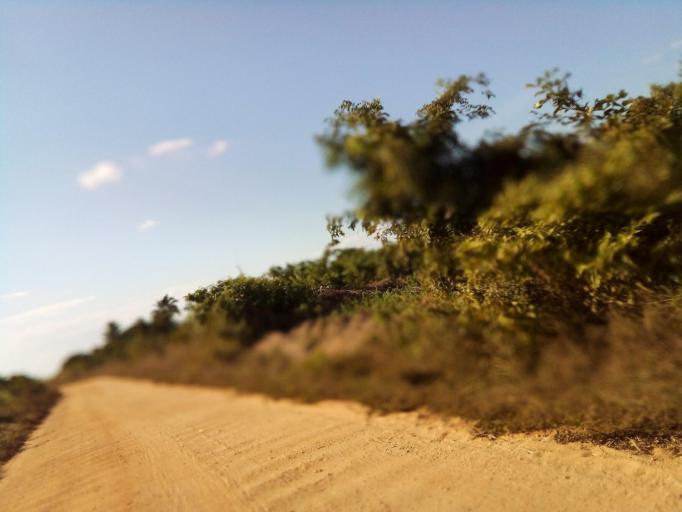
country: MZ
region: Zambezia
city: Quelimane
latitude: -17.5624
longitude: 36.6359
